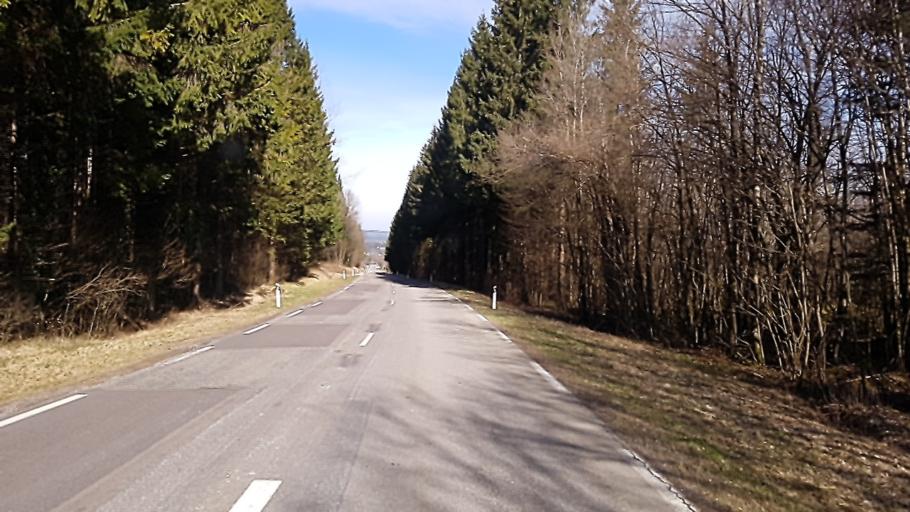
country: FR
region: Franche-Comte
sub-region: Departement du Jura
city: Champagnole
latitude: 46.7112
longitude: 5.9292
